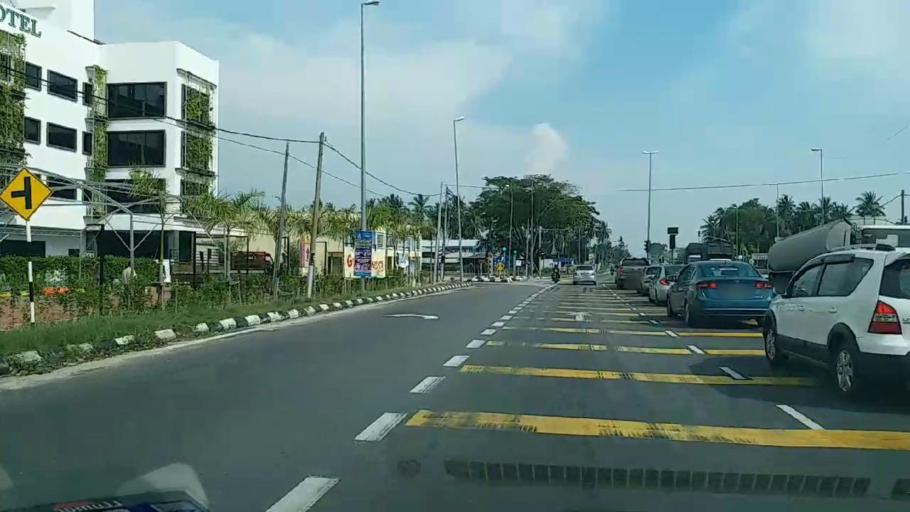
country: MY
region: Selangor
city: Kuala Selangor
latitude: 3.3552
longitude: 101.2530
